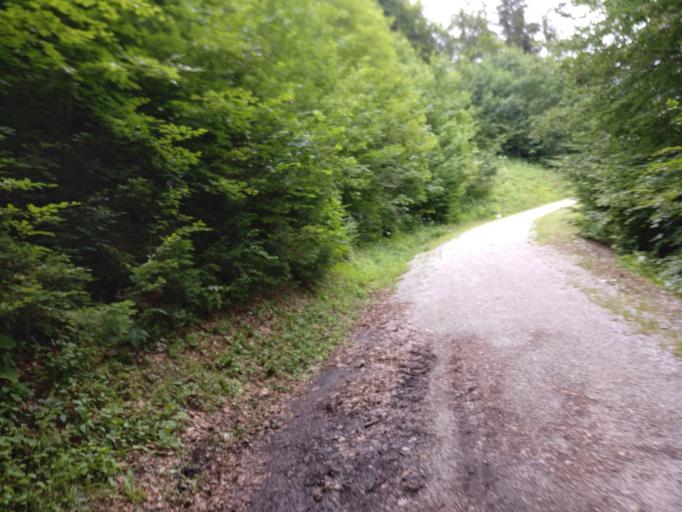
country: AT
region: Tyrol
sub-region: Politischer Bezirk Kitzbuhel
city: Hochfilzen
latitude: 47.4939
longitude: 12.6093
